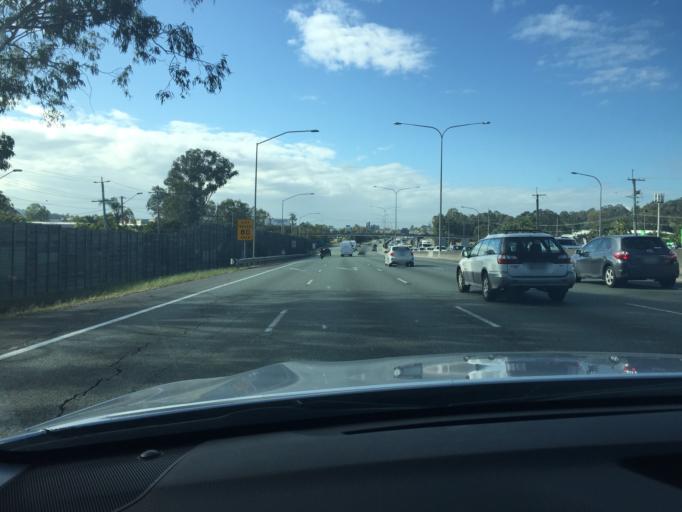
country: AU
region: Queensland
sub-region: Logan
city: Slacks Creek
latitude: -27.6544
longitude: 153.1634
